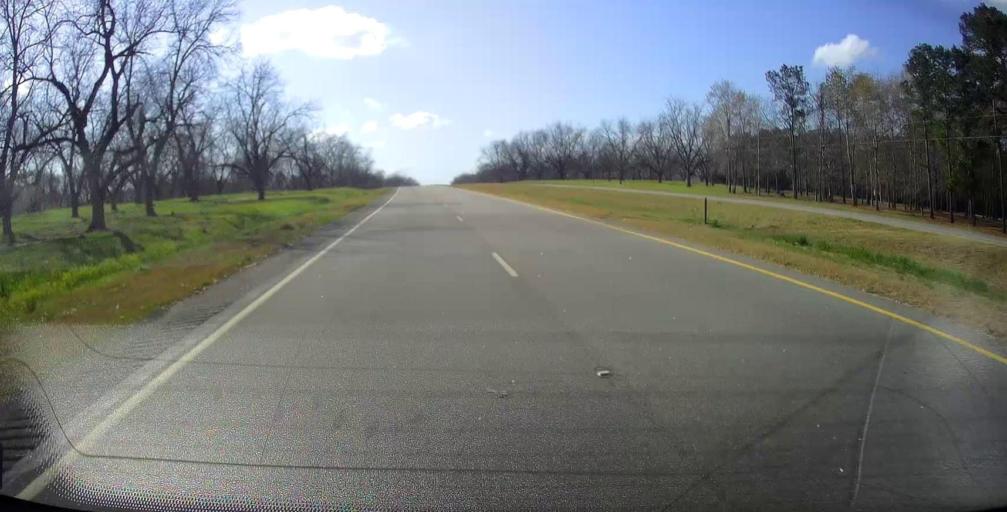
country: US
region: Georgia
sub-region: Dodge County
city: Eastman
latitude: 32.1980
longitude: -83.2210
